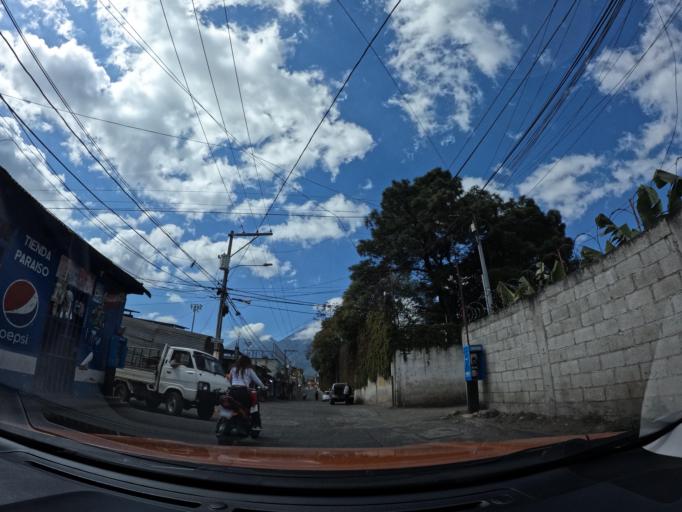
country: GT
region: Sacatepequez
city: Ciudad Vieja
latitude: 14.5250
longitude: -90.7577
